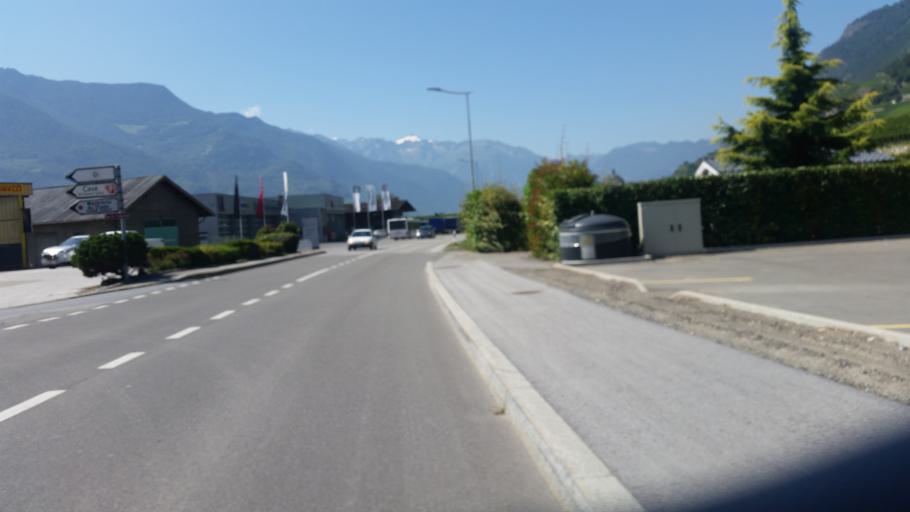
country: CH
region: Valais
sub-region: Martigny District
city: Leytron
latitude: 46.1819
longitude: 7.2024
